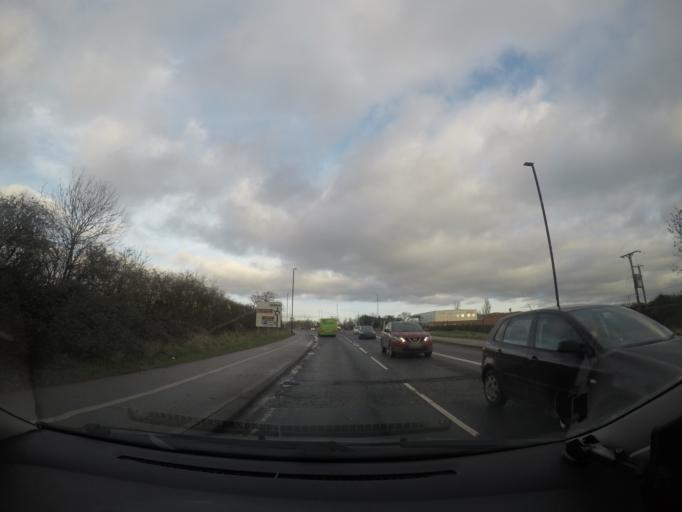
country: GB
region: England
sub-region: City of York
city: Huntington
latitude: 53.9789
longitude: -1.0505
